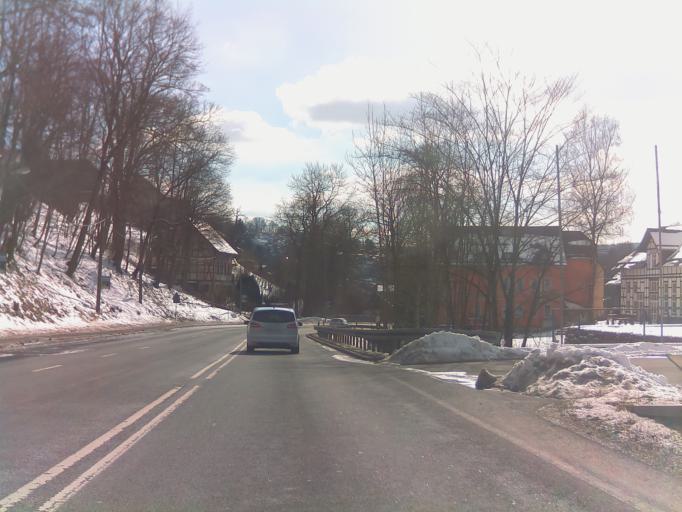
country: DE
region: Thuringia
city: Suhl
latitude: 50.6224
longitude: 10.6991
